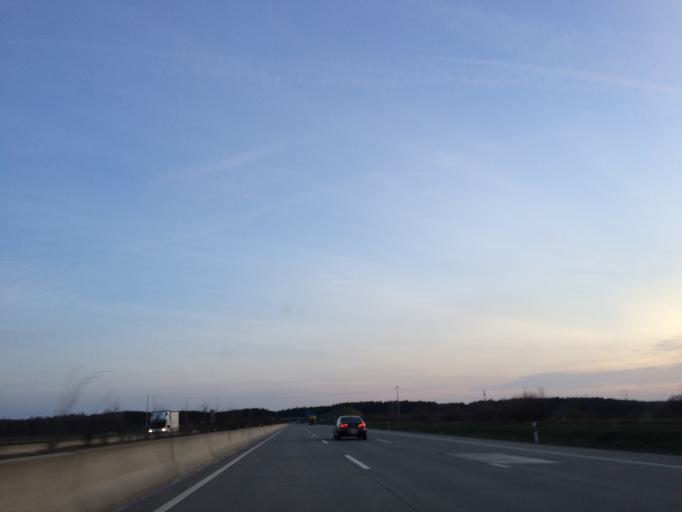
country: DE
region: Thuringia
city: Tautendorf
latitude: 50.7983
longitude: 11.8954
